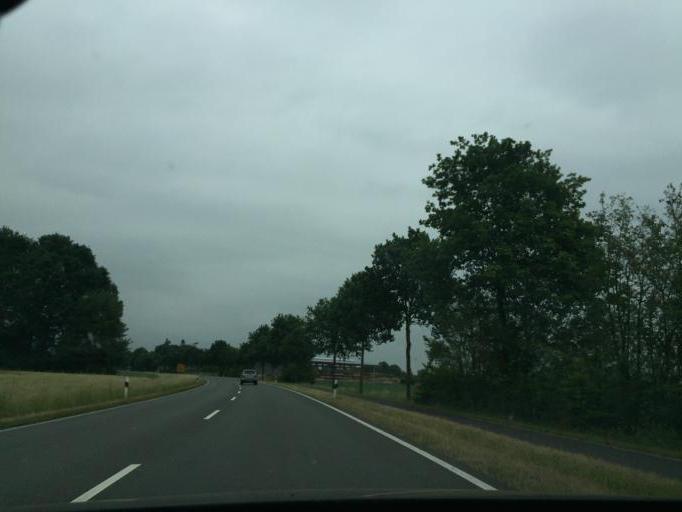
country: DE
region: North Rhine-Westphalia
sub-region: Regierungsbezirk Munster
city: Ostbevern
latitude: 52.1151
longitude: 7.8443
